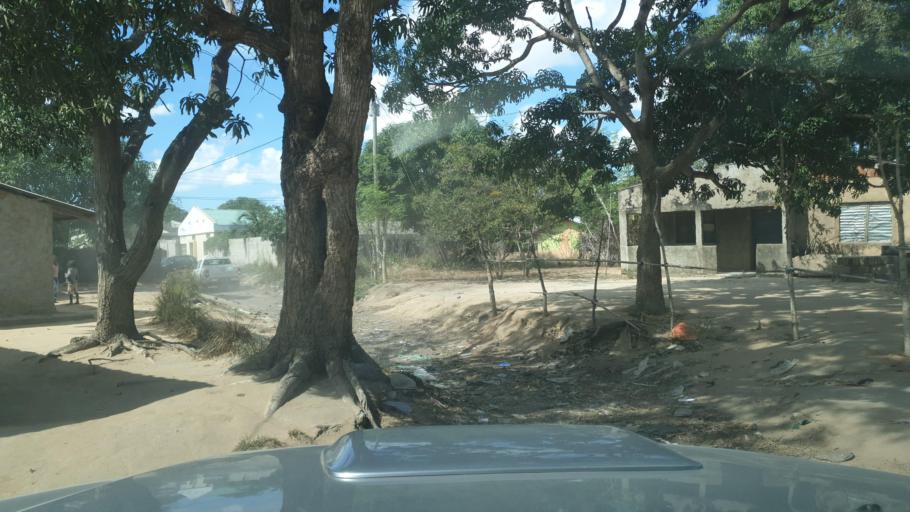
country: MZ
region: Nampula
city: Nacala
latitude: -14.5730
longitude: 40.6993
